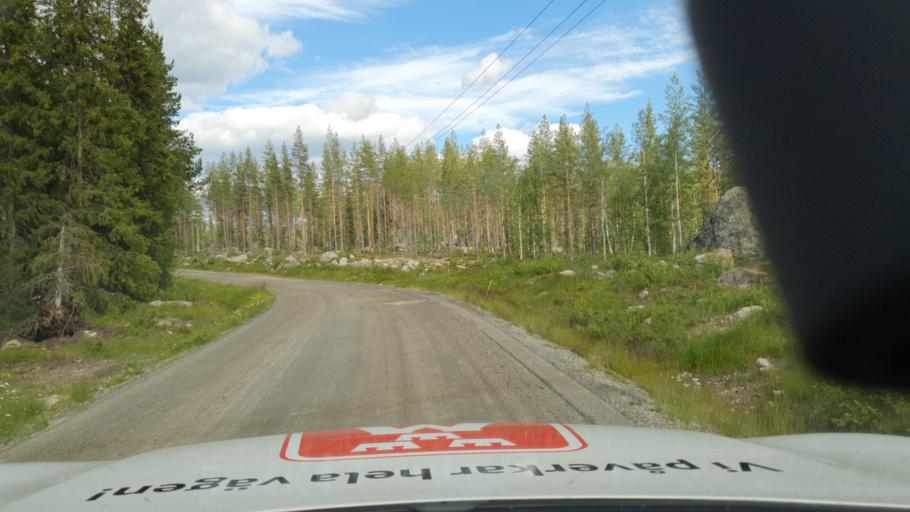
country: SE
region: Vaesterbotten
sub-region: Lycksele Kommun
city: Soderfors
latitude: 64.2761
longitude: 18.1516
